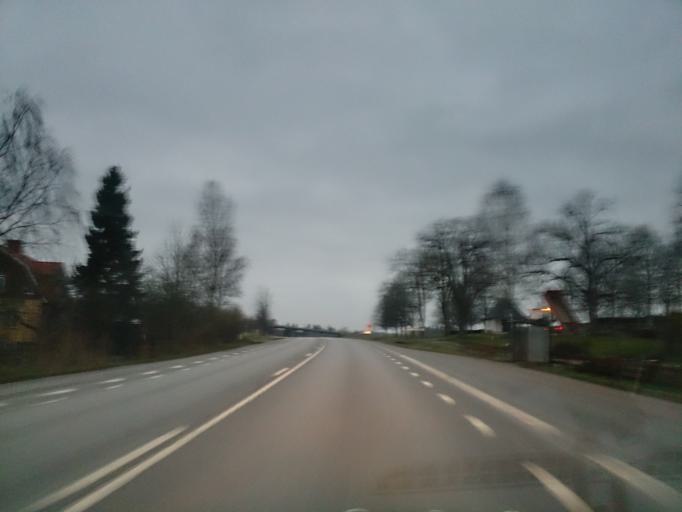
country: SE
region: OEstergoetland
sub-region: Linkopings Kommun
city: Linghem
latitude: 58.4511
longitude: 15.8319
